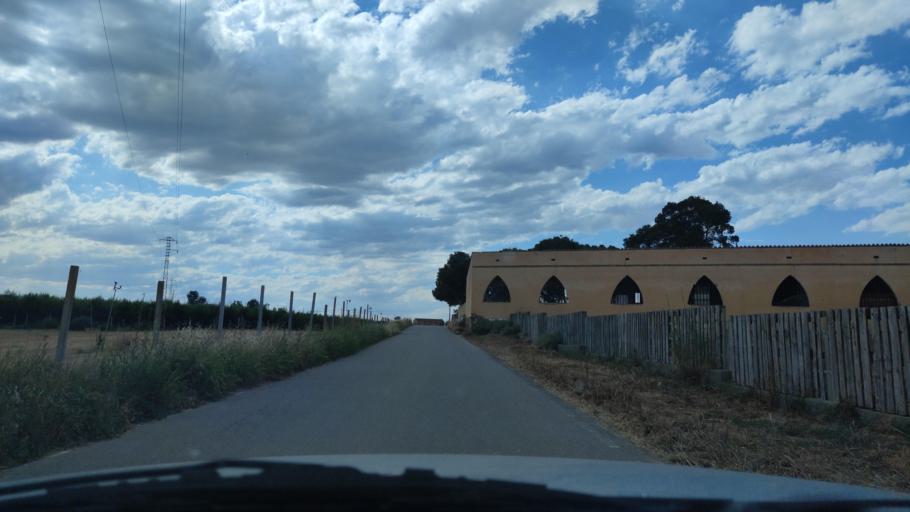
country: ES
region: Catalonia
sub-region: Provincia de Lleida
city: Alcarras
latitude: 41.5992
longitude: 0.5622
